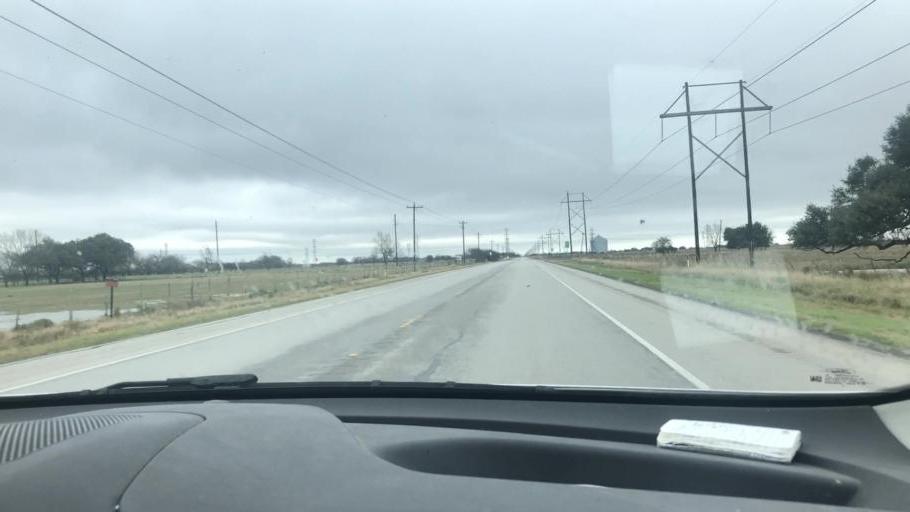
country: US
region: Texas
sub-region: Wharton County
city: Boling
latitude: 29.1849
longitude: -96.0101
